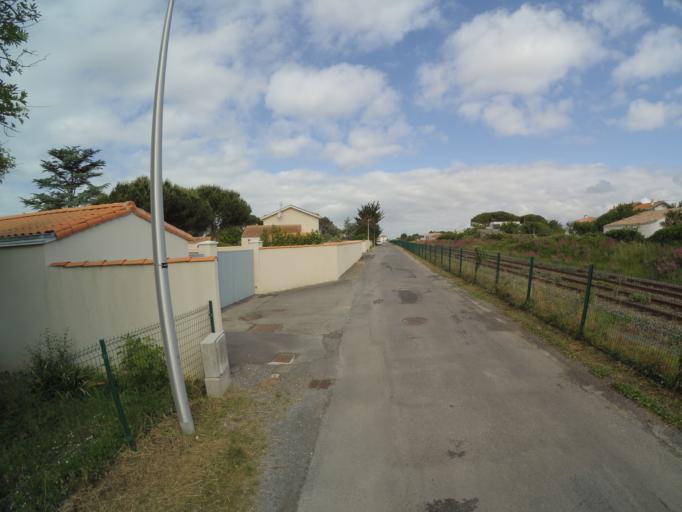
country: FR
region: Poitou-Charentes
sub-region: Departement de la Charente-Maritime
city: Angoulins
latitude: 46.0979
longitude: -1.1059
